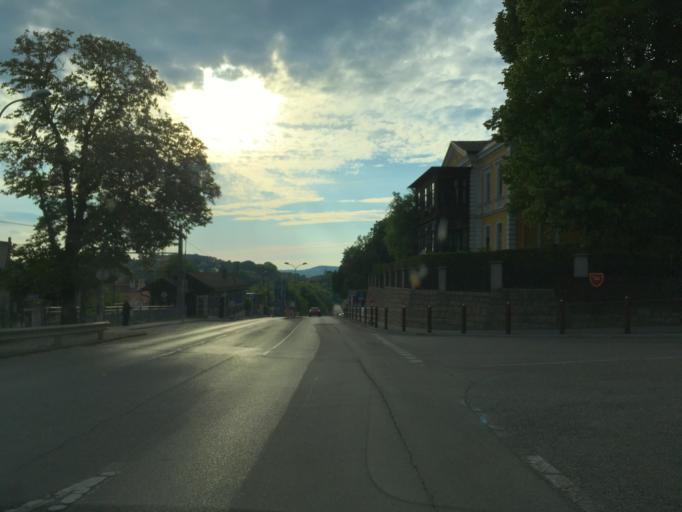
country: AT
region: Lower Austria
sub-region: Politischer Bezirk Sankt Polten
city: Neulengbach
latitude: 48.1963
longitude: 15.9075
